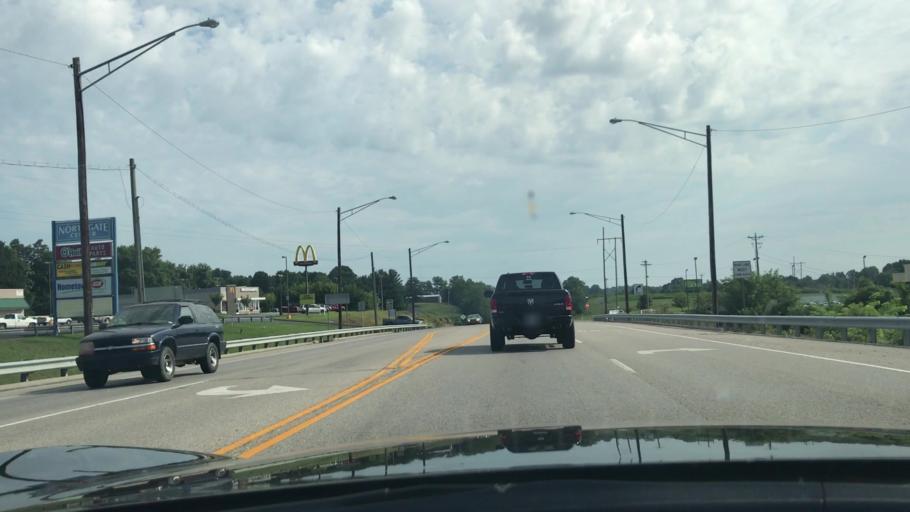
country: US
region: Kentucky
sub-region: Green County
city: Greensburg
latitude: 37.2714
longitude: -85.4958
